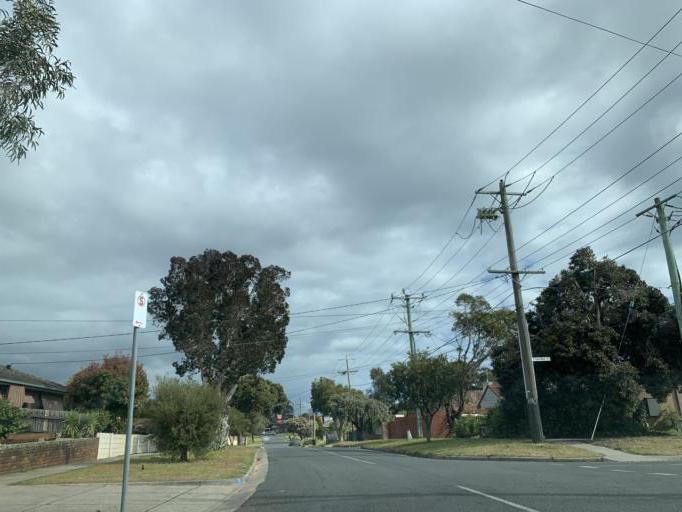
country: AU
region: Victoria
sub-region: Kingston
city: Mentone
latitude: -37.9806
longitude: 145.0764
